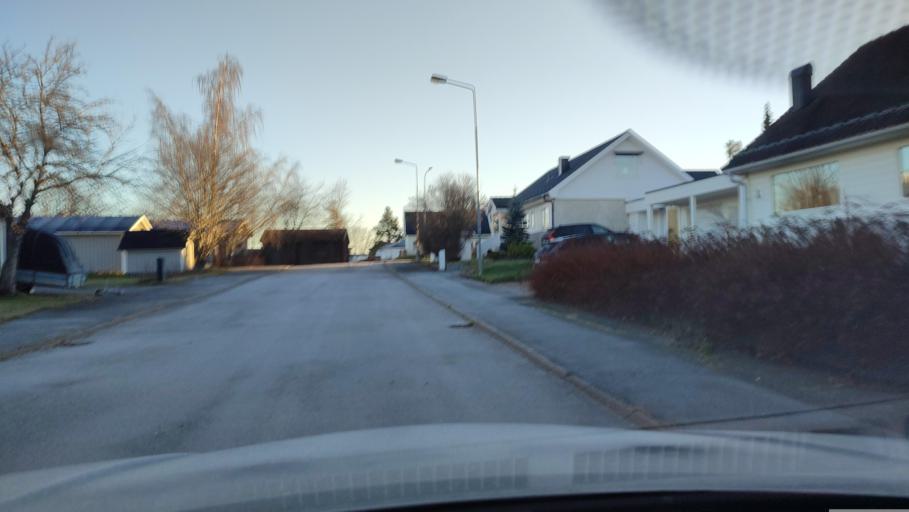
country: SE
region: Vaesterbotten
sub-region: Skelleftea Kommun
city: Viken
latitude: 64.7459
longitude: 20.9184
